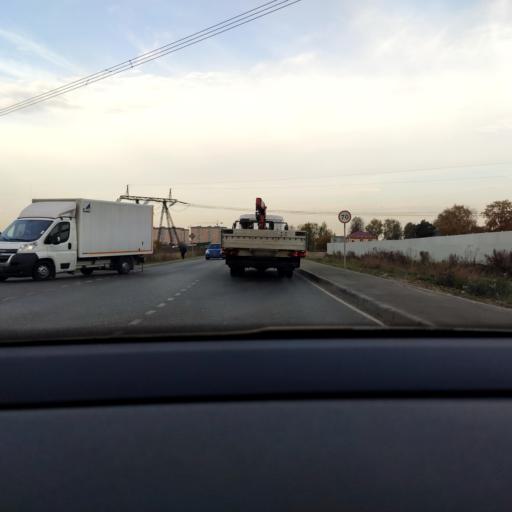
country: RU
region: Moskovskaya
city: Pirogovskiy
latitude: 55.9694
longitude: 37.7567
